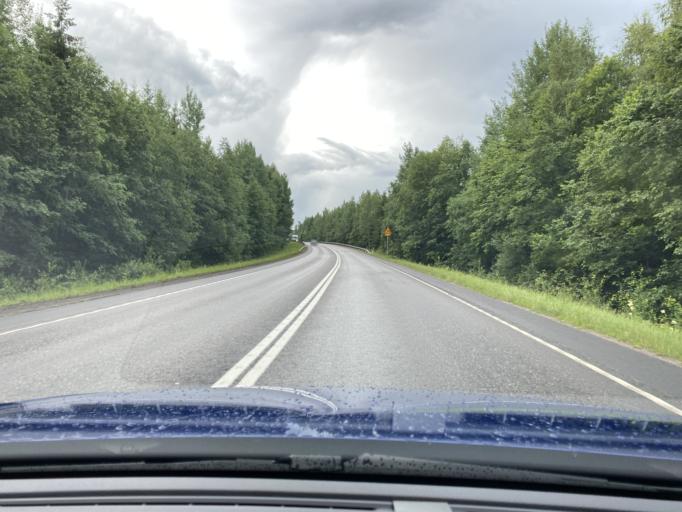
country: FI
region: Uusimaa
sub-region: Helsinki
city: Hyvinge
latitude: 60.5746
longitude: 24.7984
